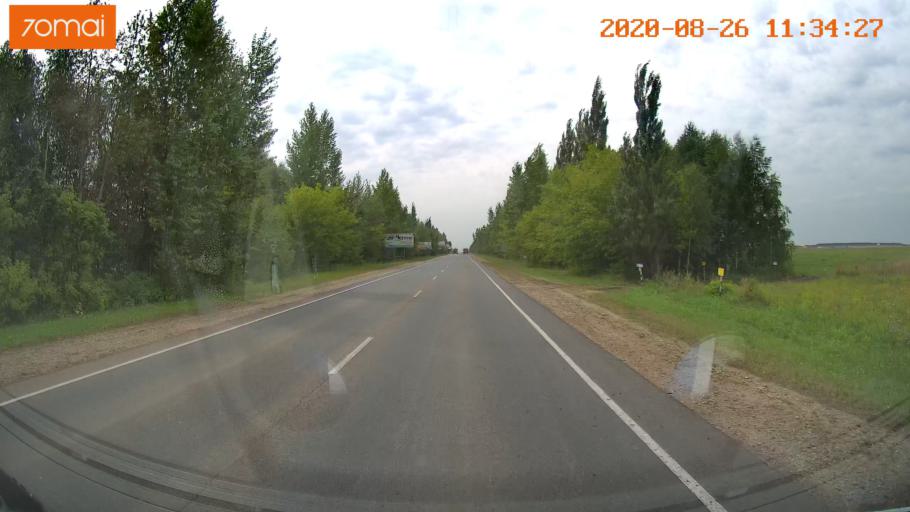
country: RU
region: Rjazan
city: Shilovo
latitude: 54.2858
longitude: 40.8438
